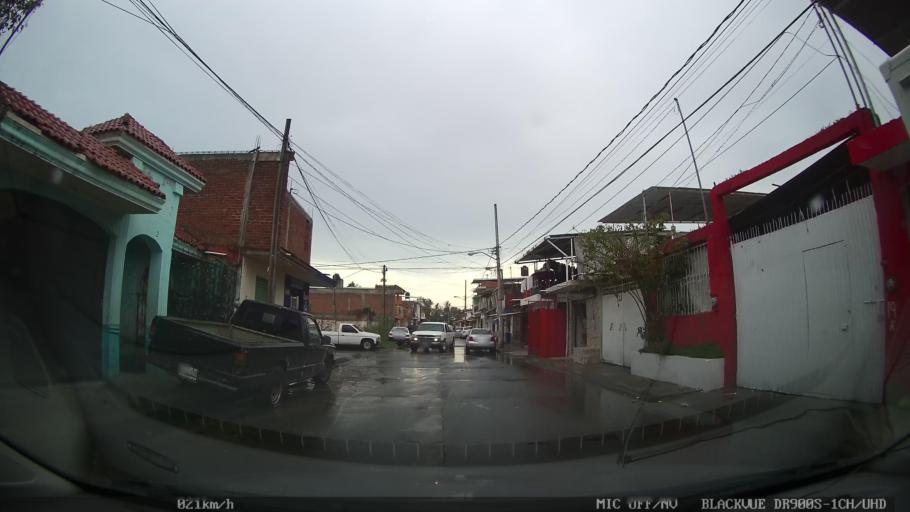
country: MX
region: Michoacan
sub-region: Uruapan
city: Santa Rosa (Santa Barbara)
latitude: 19.4009
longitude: -102.0267
